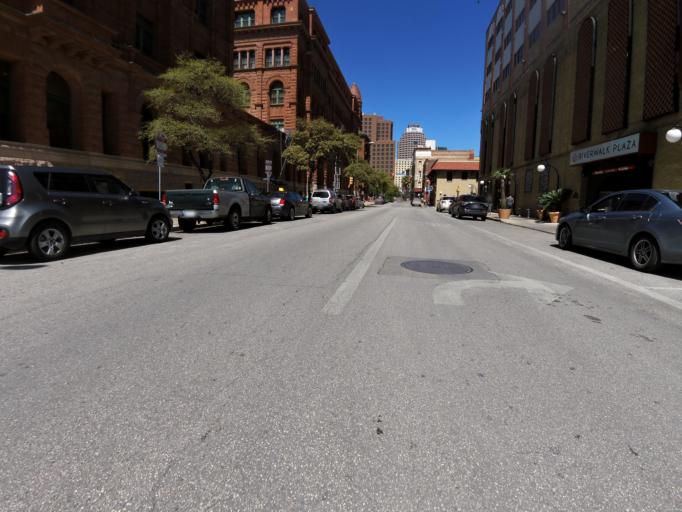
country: US
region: Texas
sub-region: Bexar County
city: San Antonio
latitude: 29.4226
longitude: -98.4934
